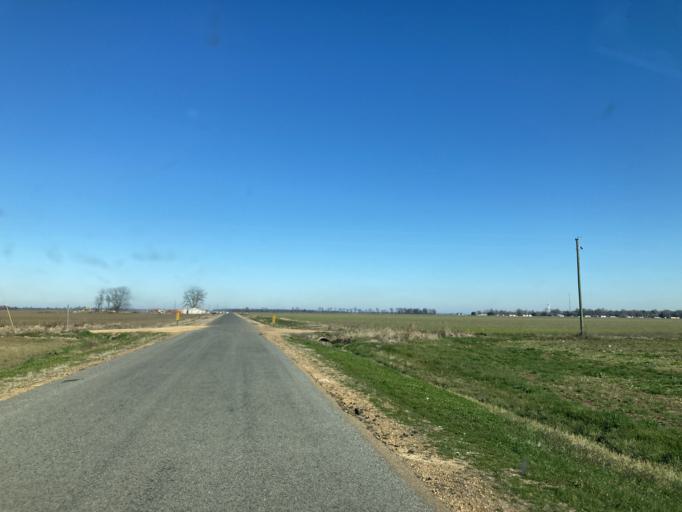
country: US
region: Mississippi
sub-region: Yazoo County
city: Yazoo City
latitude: 32.9660
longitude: -90.6055
